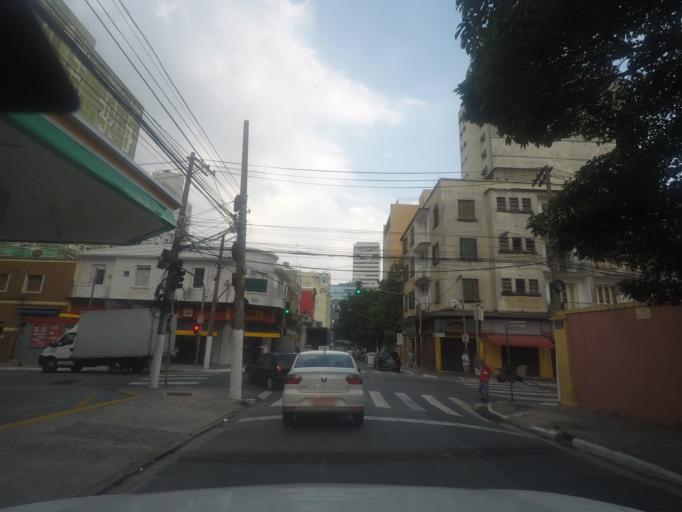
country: BR
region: Sao Paulo
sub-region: Sao Paulo
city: Sao Paulo
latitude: -23.5528
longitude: -46.6434
